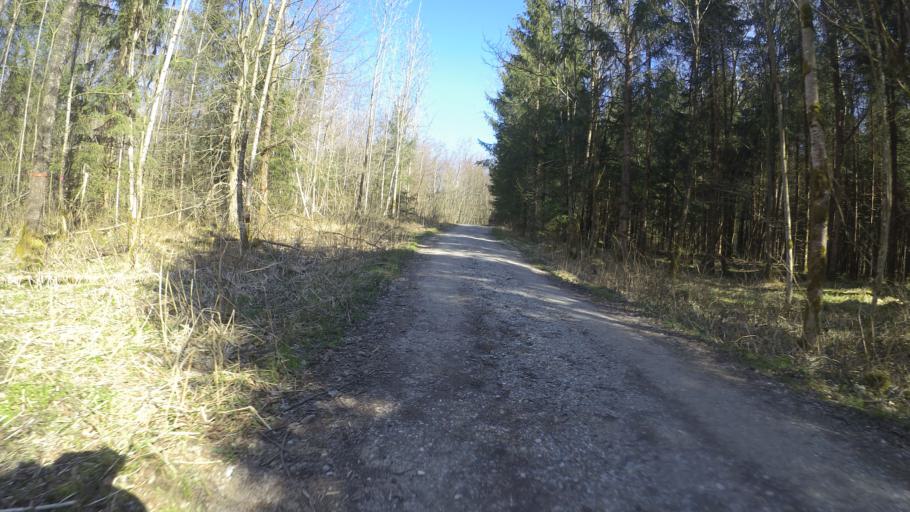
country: DE
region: Bavaria
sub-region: Upper Bavaria
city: Seeon-Seebruck
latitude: 47.9603
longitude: 12.4841
